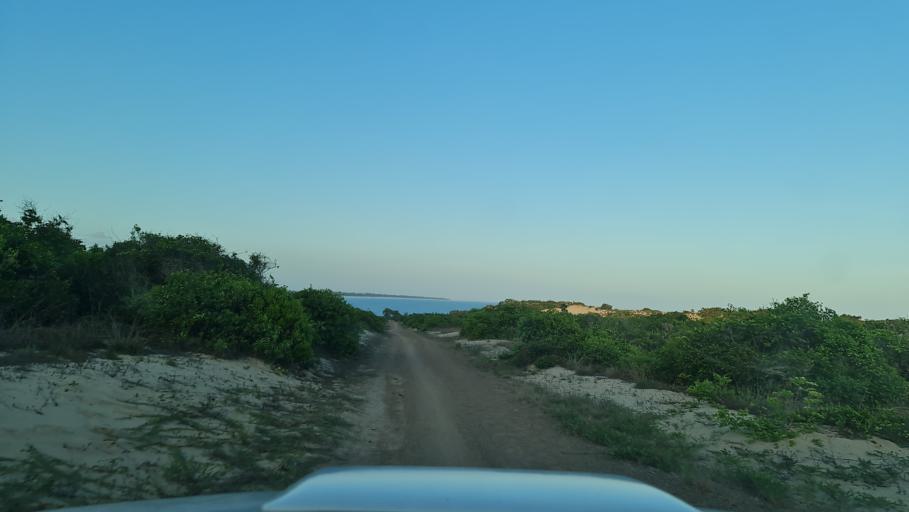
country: MZ
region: Nampula
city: Ilha de Mocambique
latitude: -15.6312
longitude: 40.4196
